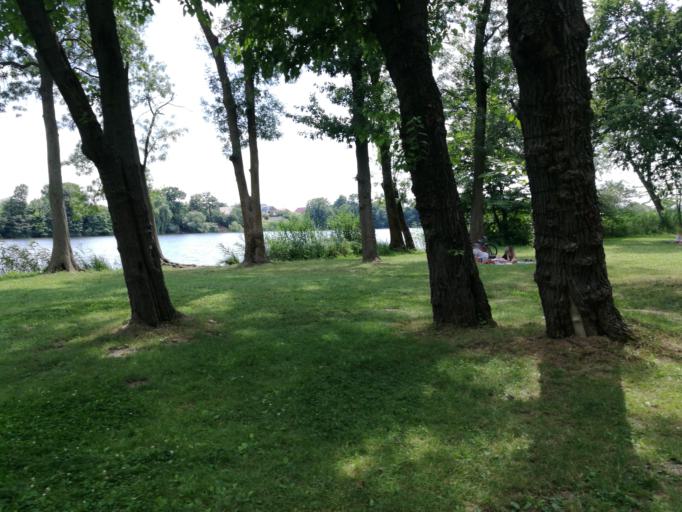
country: RO
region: Ilfov
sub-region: Comuna Mogosoaia
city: Mogosoaia
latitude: 44.5244
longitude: 25.9986
